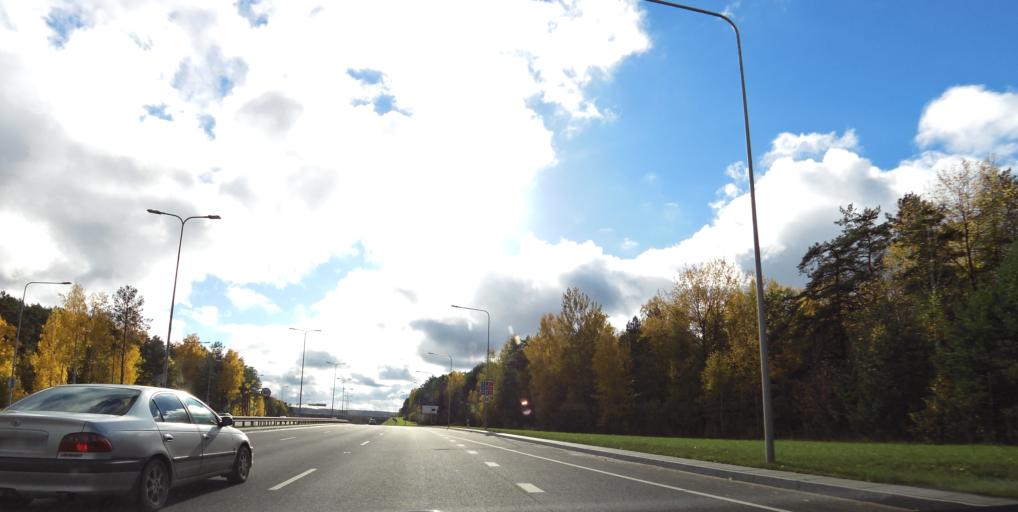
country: LT
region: Vilnius County
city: Lazdynai
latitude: 54.6810
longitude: 25.1942
